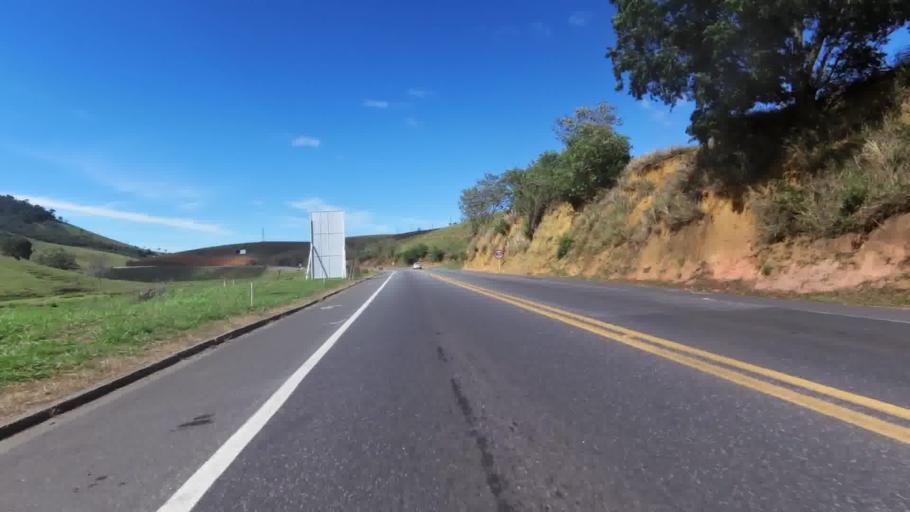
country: BR
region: Espirito Santo
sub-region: Iconha
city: Iconha
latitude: -20.7503
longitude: -40.7601
